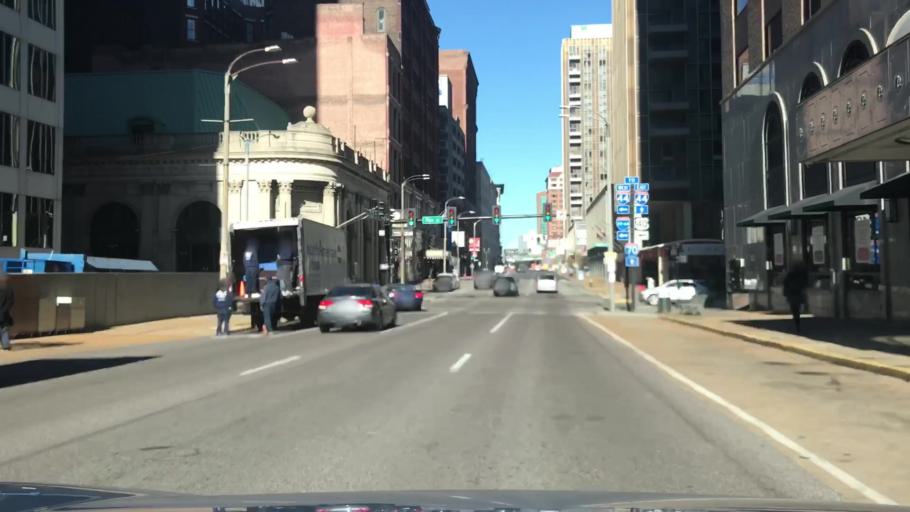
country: US
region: Missouri
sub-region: City of Saint Louis
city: St. Louis
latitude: 38.6263
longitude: -90.1883
